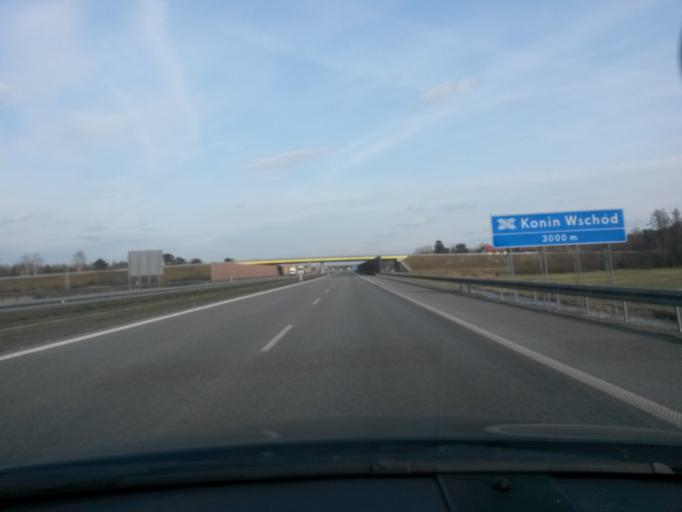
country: PL
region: Greater Poland Voivodeship
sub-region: Powiat koninski
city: Stare Miasto
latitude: 52.1612
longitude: 18.2255
